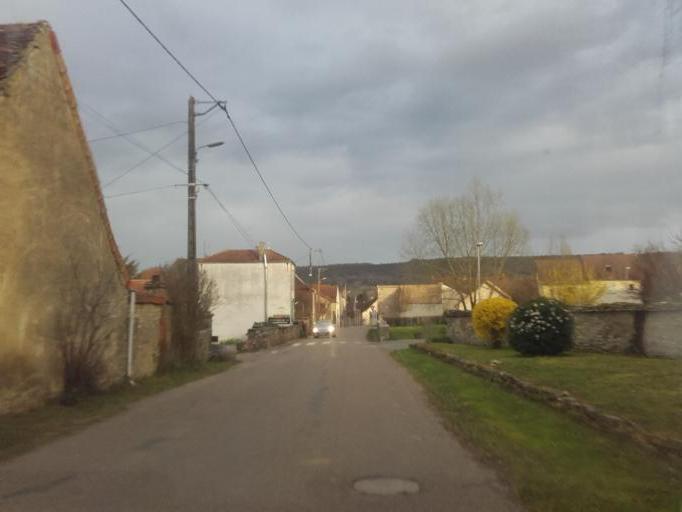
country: FR
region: Bourgogne
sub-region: Departement de Saone-et-Loire
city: Saint-Leger-sur-Dheune
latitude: 46.8979
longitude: 4.6660
